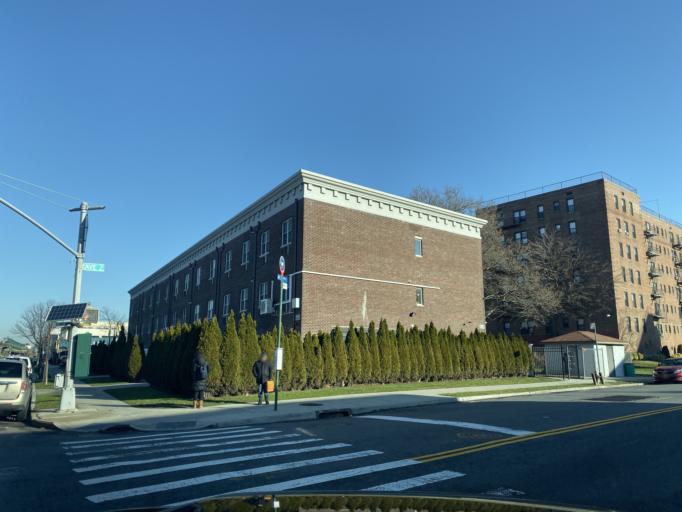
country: US
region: New York
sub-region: Kings County
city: Coney Island
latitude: 40.5858
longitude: -73.9742
